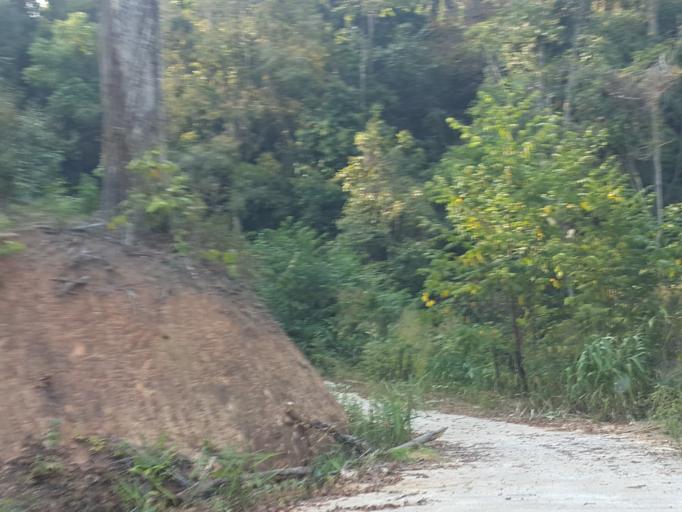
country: TH
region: Chiang Mai
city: Samoeng
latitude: 19.0207
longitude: 98.7627
